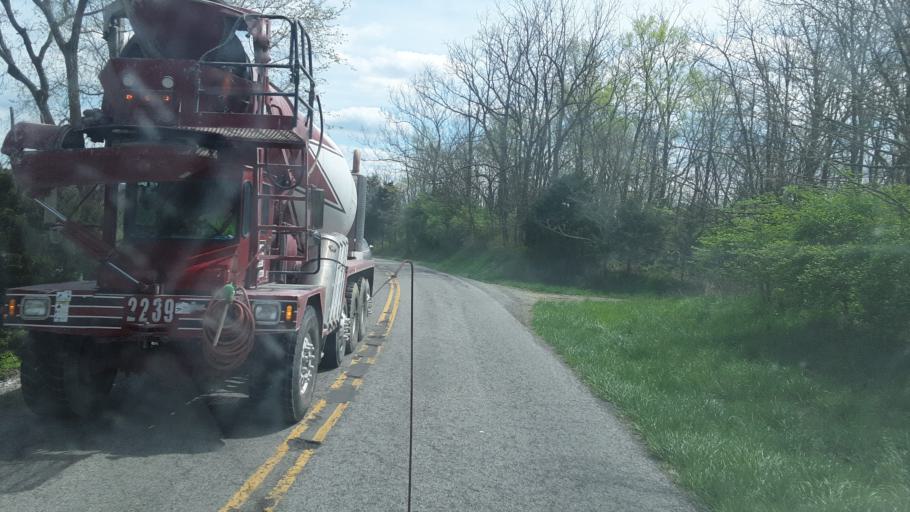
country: US
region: Kentucky
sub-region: Grant County
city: Dry Ridge
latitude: 38.6477
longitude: -84.7365
